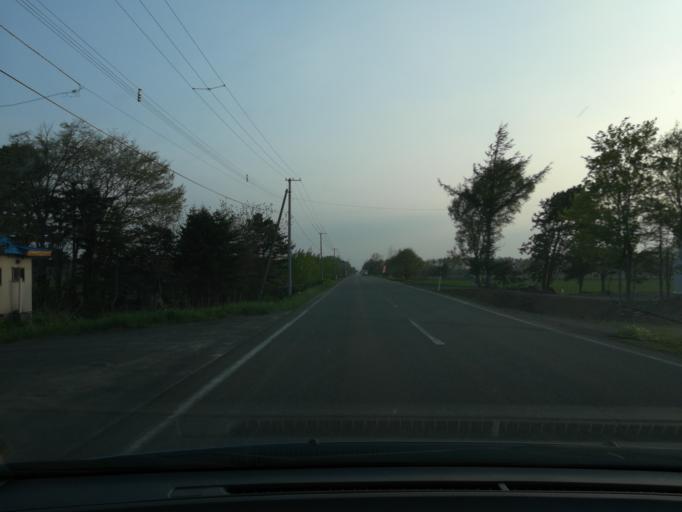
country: JP
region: Hokkaido
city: Ebetsu
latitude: 43.0935
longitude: 141.6392
